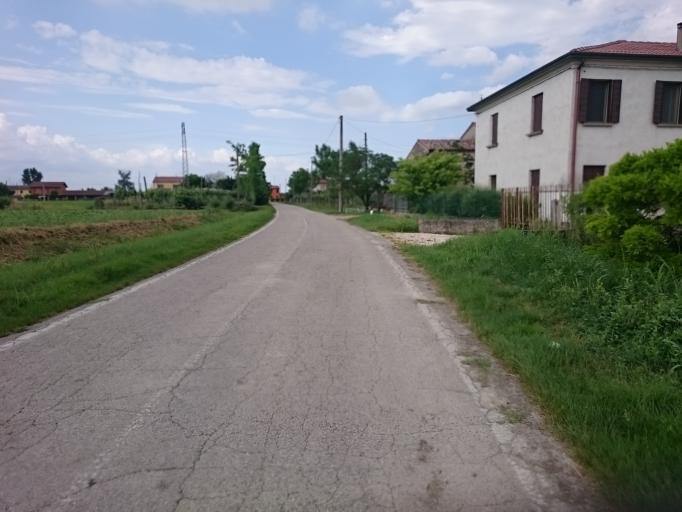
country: IT
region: Veneto
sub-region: Provincia di Padova
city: Ponso
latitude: 45.1983
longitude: 11.5735
